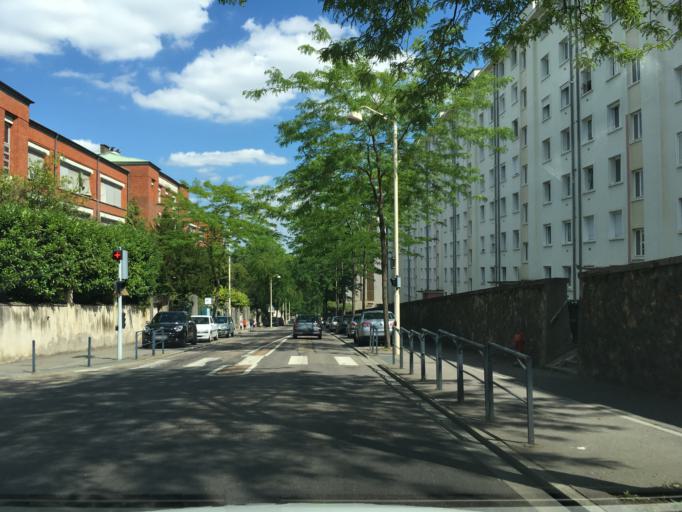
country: FR
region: Lorraine
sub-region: Departement de Meurthe-et-Moselle
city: Laxou
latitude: 48.6920
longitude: 6.1484
